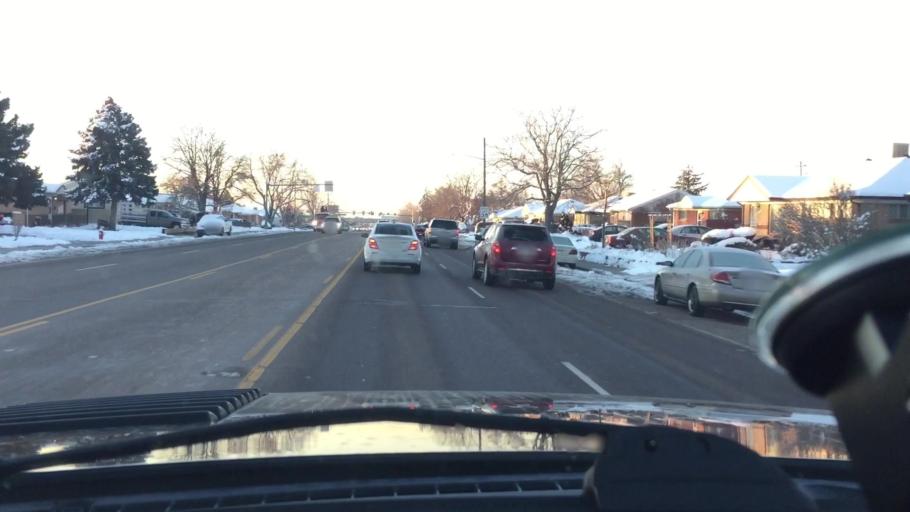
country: US
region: Colorado
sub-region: Adams County
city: Sherrelwood
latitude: 39.8373
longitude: -105.0061
